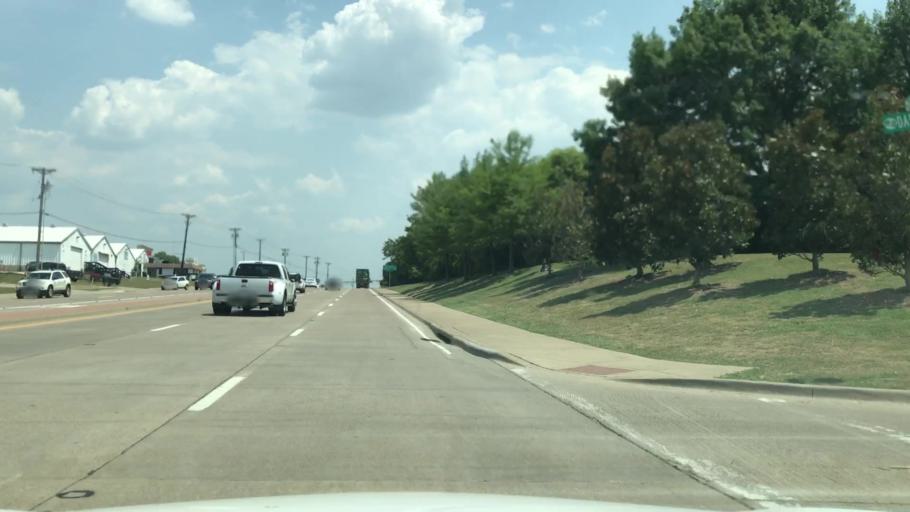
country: US
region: Texas
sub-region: Rockwall County
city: Rockwall
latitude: 32.9153
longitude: -96.4551
